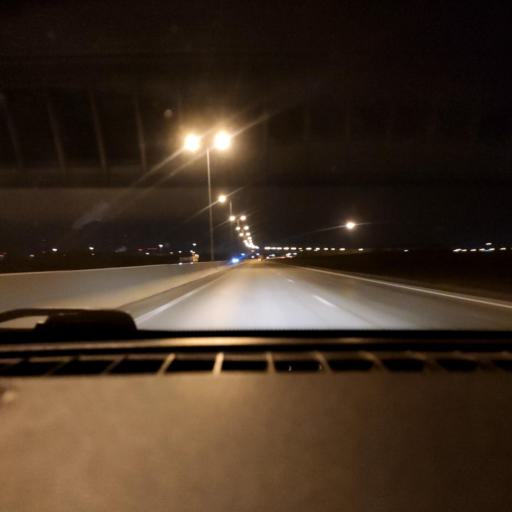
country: RU
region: Perm
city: Froly
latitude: 57.9286
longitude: 56.1824
